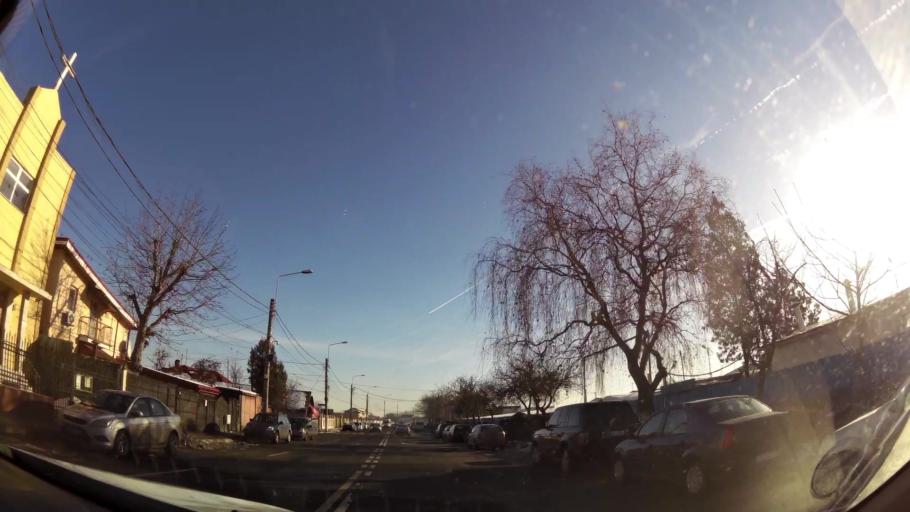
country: RO
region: Ilfov
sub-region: Comuna Fundeni-Dobroesti
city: Fundeni
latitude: 44.4768
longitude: 26.1392
